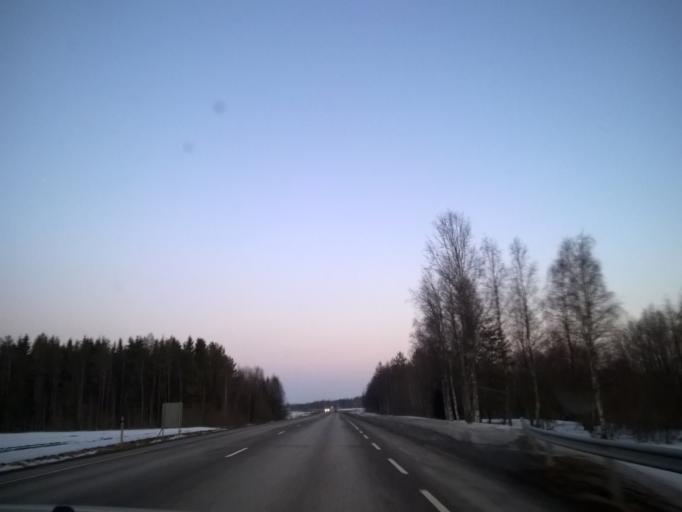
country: FI
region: Northern Ostrobothnia
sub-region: Nivala-Haapajaervi
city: Kaersaemaeki
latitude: 63.8399
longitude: 25.8573
